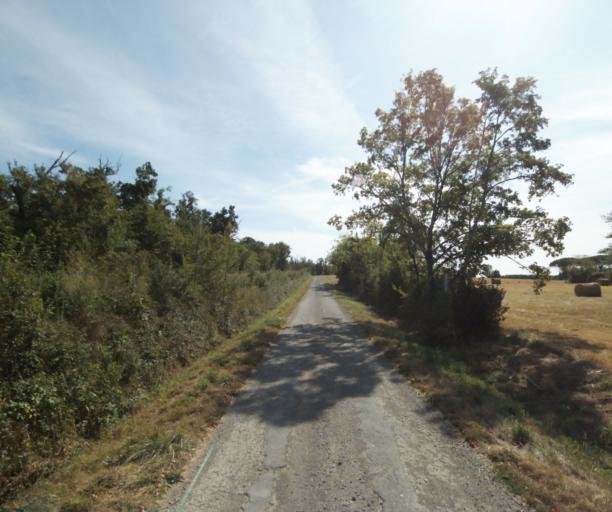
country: FR
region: Midi-Pyrenees
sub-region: Departement du Tarn
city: Soual
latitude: 43.5191
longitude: 2.0935
